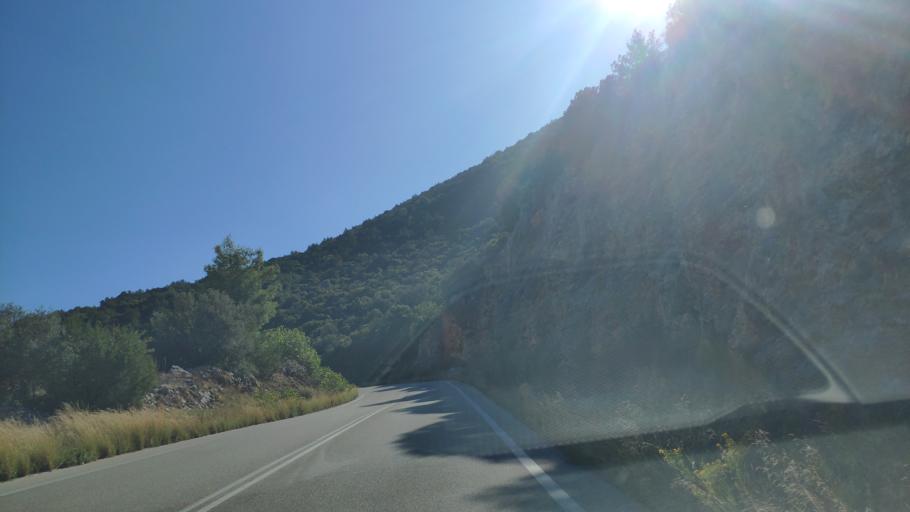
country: GR
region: Peloponnese
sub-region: Nomos Argolidos
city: Palaia Epidavros
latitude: 37.6249
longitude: 23.1448
